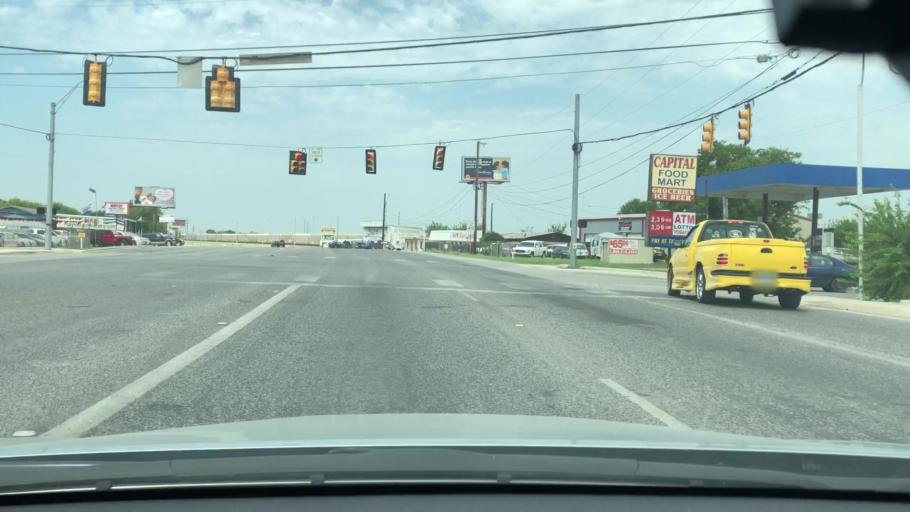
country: US
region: Texas
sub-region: Bexar County
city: Kirby
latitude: 29.4747
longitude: -98.3809
